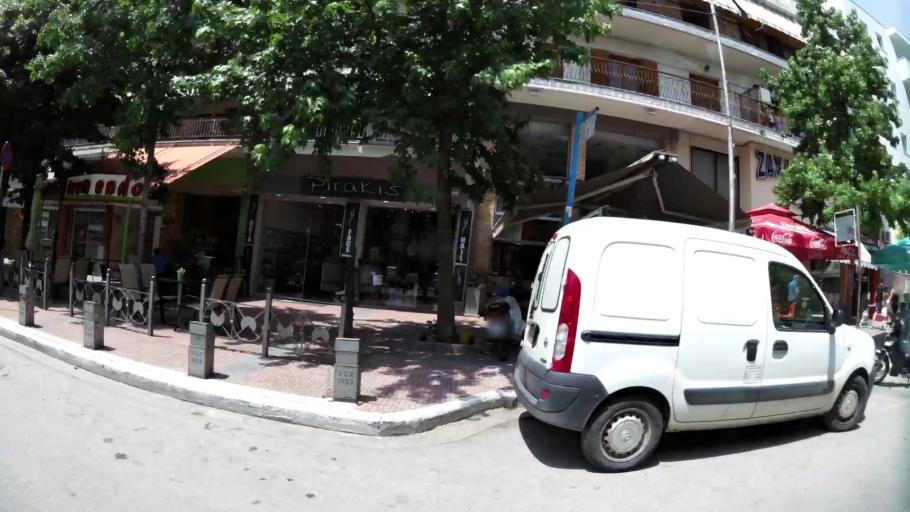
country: GR
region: Central Macedonia
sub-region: Nomos Thessalonikis
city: Menemeni
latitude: 40.6695
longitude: 22.8943
